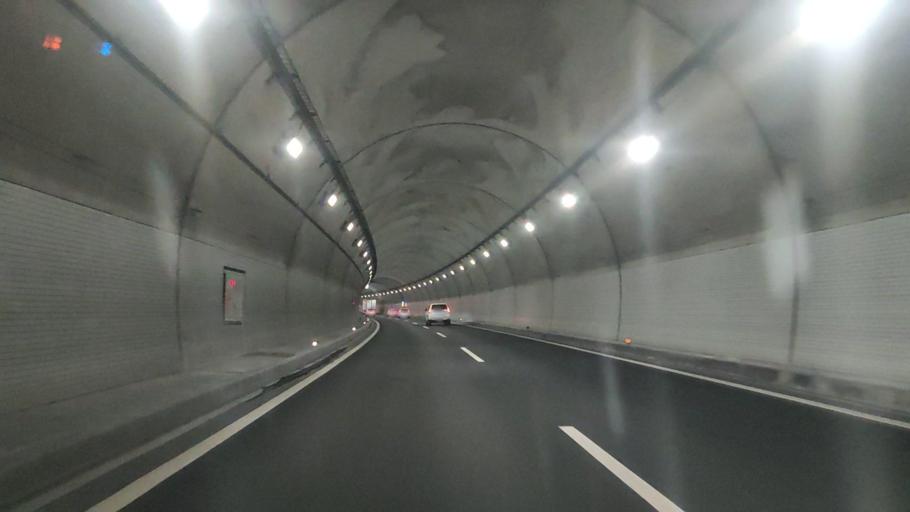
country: JP
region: Fukuoka
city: Kanda
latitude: 33.8031
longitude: 130.9456
